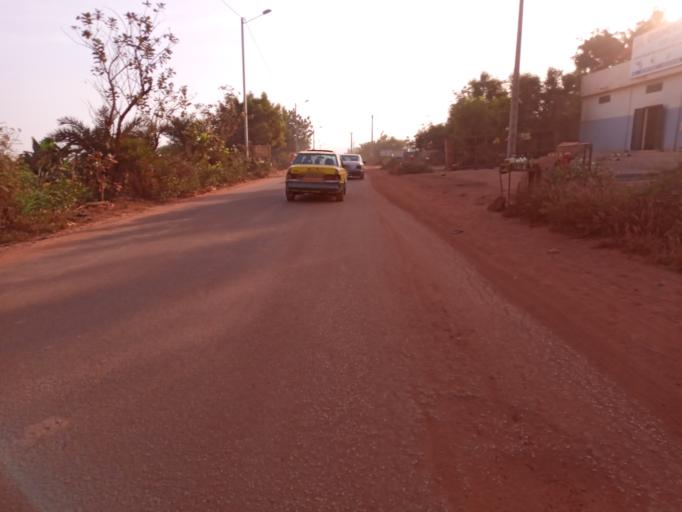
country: ML
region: Bamako
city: Bamako
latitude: 12.6347
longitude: -7.9344
